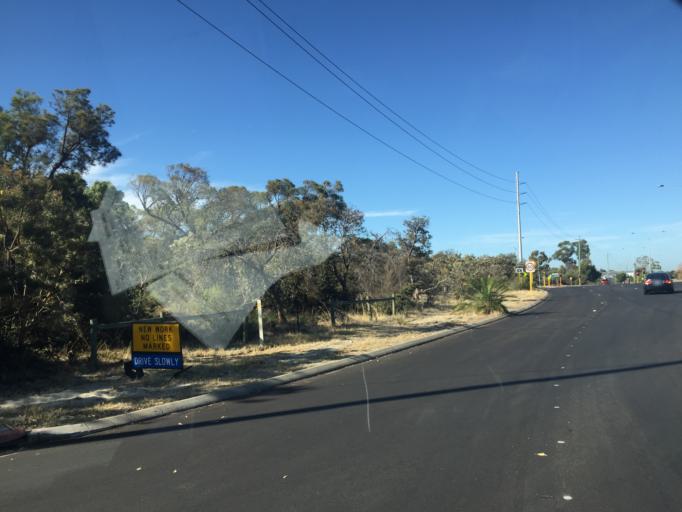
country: AU
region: Western Australia
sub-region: Canning
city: East Cannington
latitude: -31.9996
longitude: 115.9623
